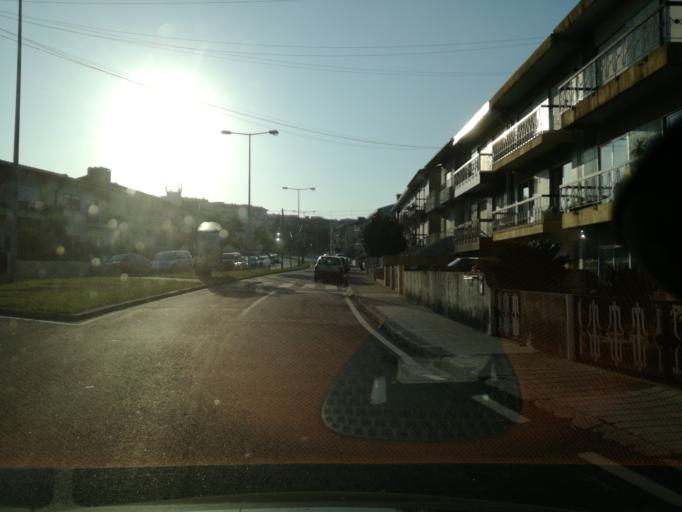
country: PT
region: Porto
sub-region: Maia
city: Milheiros
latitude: 41.2173
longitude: -8.5995
